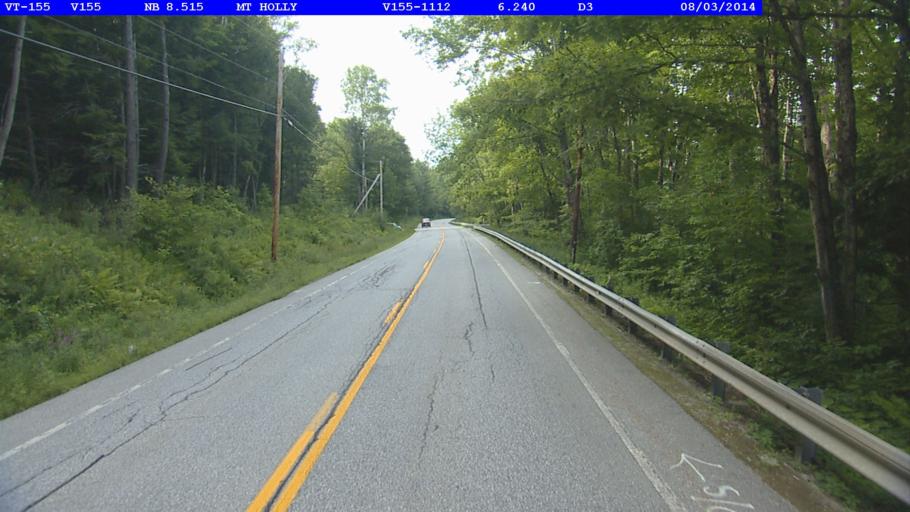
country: US
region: Vermont
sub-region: Rutland County
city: Rutland
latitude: 43.4328
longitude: -72.8579
